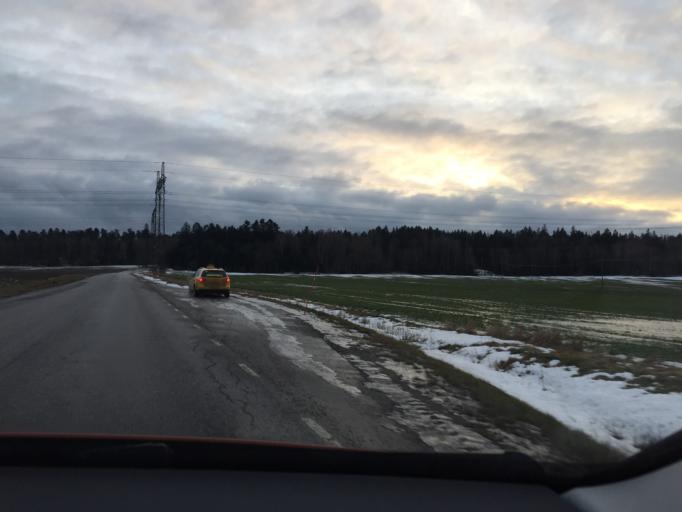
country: SE
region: Stockholm
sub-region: Botkyrka Kommun
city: Eriksberg
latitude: 59.2149
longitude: 17.7793
